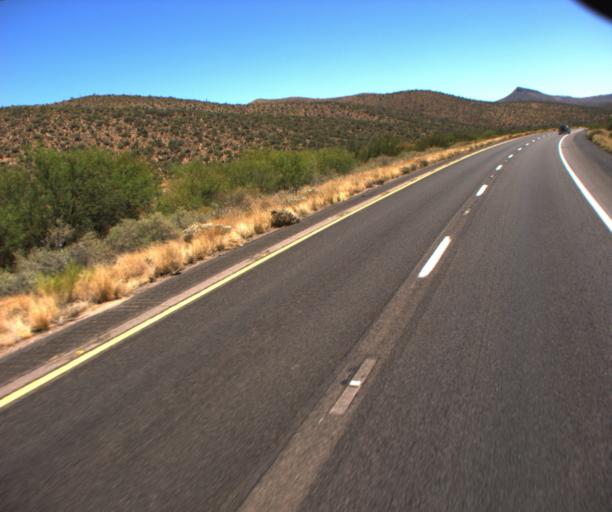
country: US
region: Arizona
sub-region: Maricopa County
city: Rio Verde
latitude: 33.7860
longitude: -111.4934
